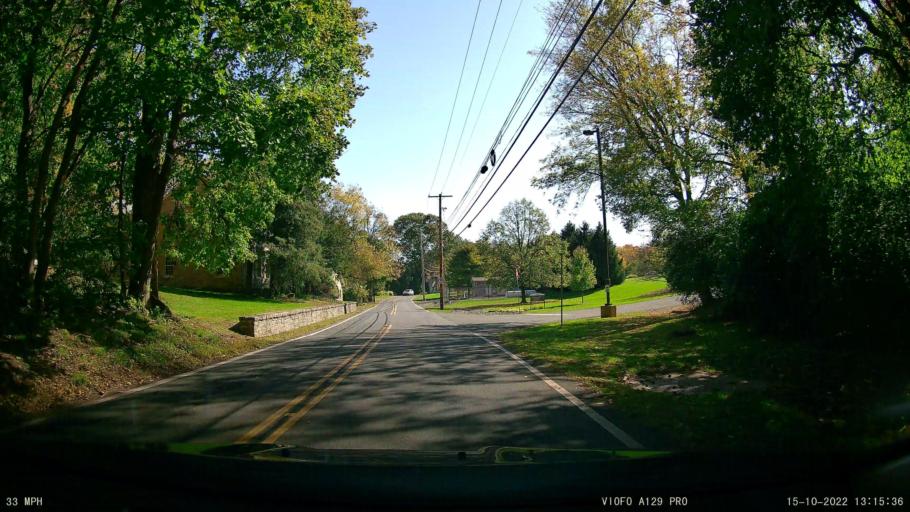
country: US
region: Pennsylvania
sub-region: Berks County
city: Spring Ridge
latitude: 40.3590
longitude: -75.9687
